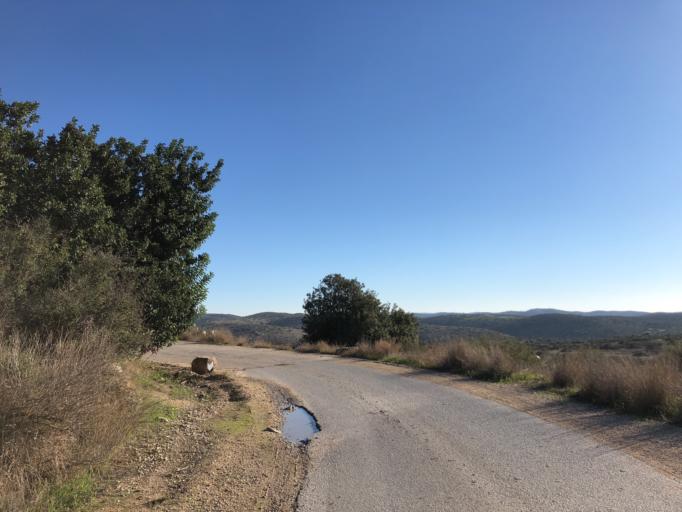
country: PS
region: West Bank
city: Idhna
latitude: 31.5923
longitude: 34.8974
